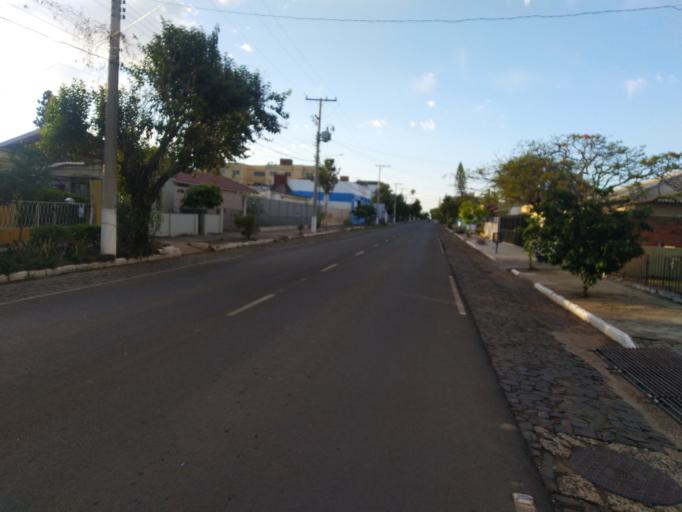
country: BR
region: Rio Grande do Sul
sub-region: Sao Borja
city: Sao Borja
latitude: -28.6547
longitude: -56.0102
